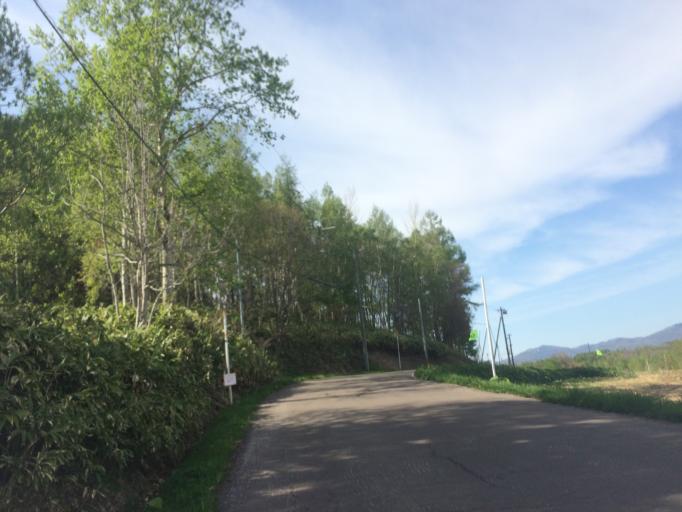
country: JP
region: Hokkaido
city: Niseko Town
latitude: 42.9064
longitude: 140.7398
